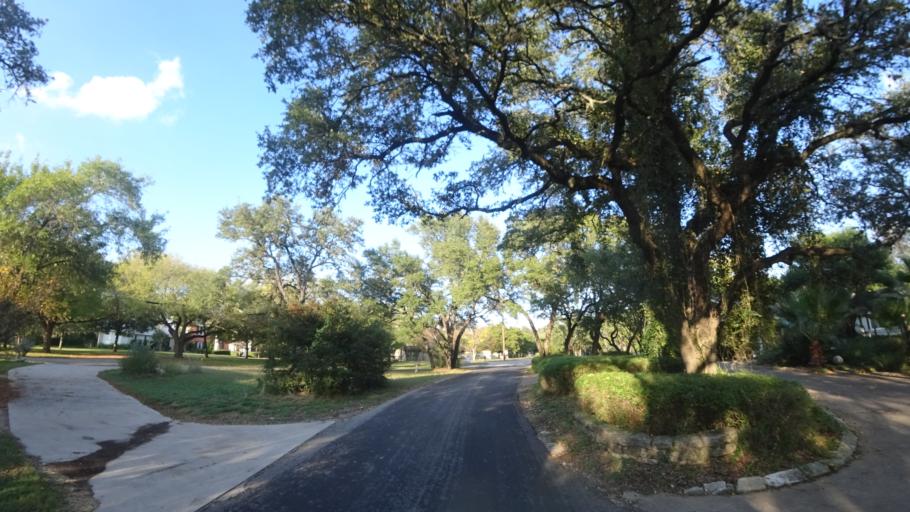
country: US
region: Texas
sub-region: Travis County
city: Lost Creek
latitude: 30.2956
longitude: -97.8449
